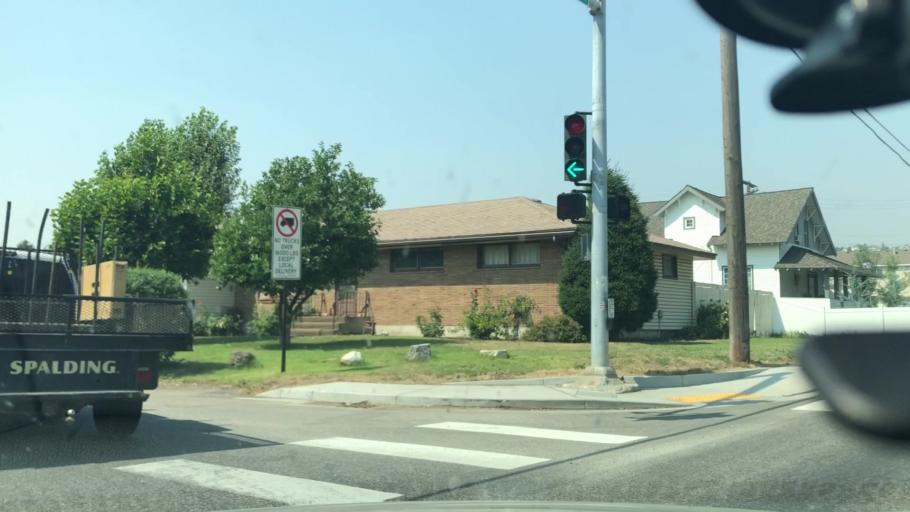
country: US
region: Washington
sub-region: Spokane County
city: Millwood
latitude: 47.6969
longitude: -117.2829
